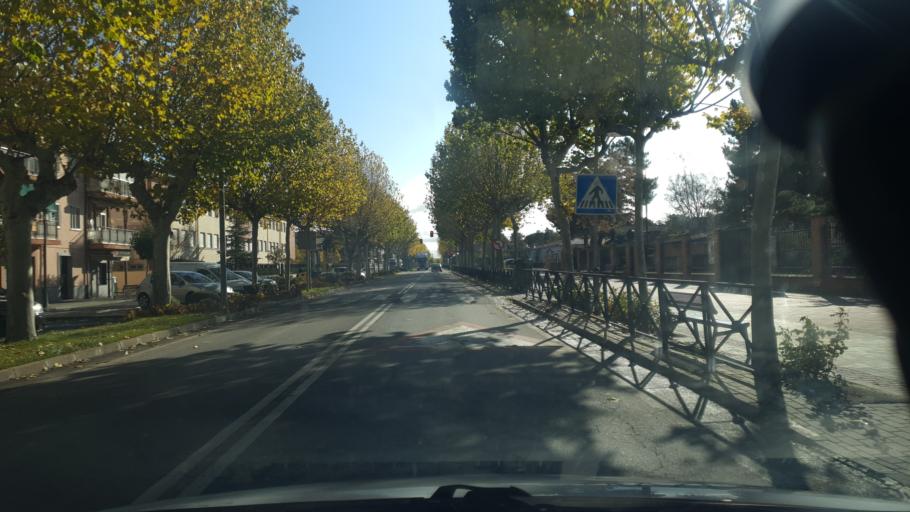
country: ES
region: Castille and Leon
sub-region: Provincia de Avila
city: Arevalo
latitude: 41.0563
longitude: -4.7147
